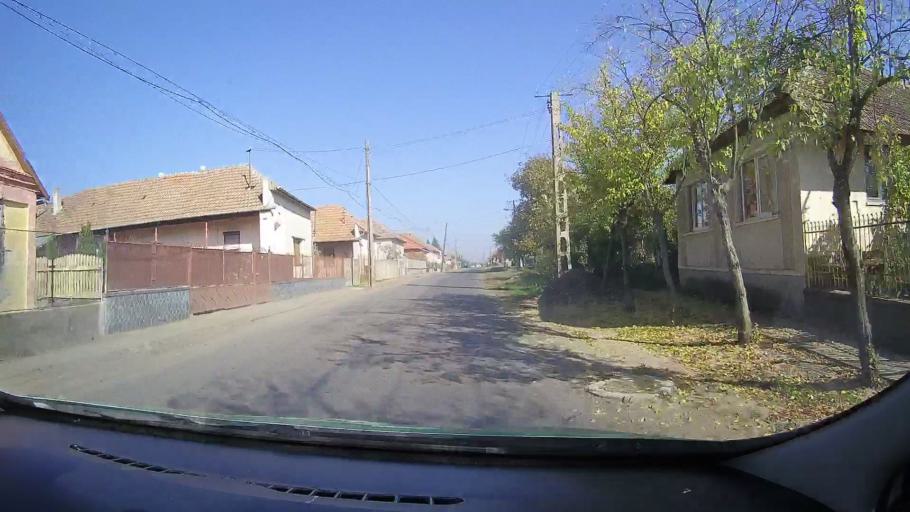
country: RO
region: Satu Mare
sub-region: Comuna Ciumesti
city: Ciumesti
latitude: 47.6574
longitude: 22.3337
